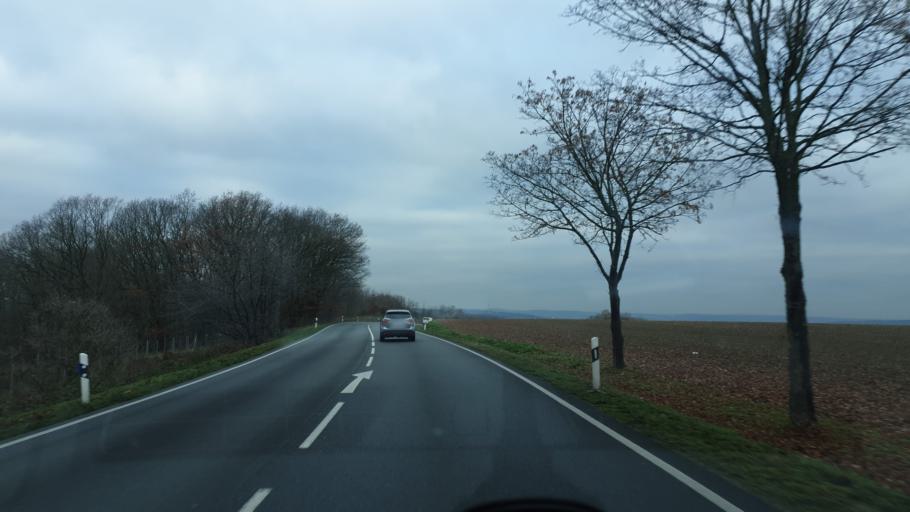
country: DE
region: Saxony-Anhalt
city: Stossen
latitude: 51.1255
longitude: 11.8998
